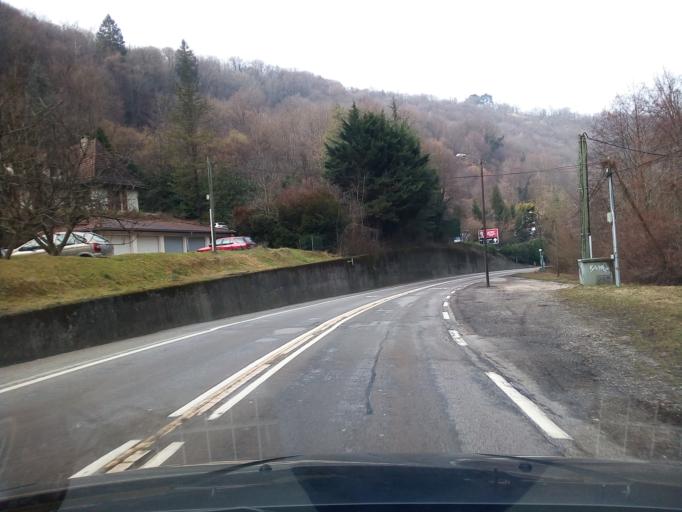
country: FR
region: Rhone-Alpes
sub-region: Departement de l'Isere
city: Gieres
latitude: 45.1698
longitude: 5.7915
